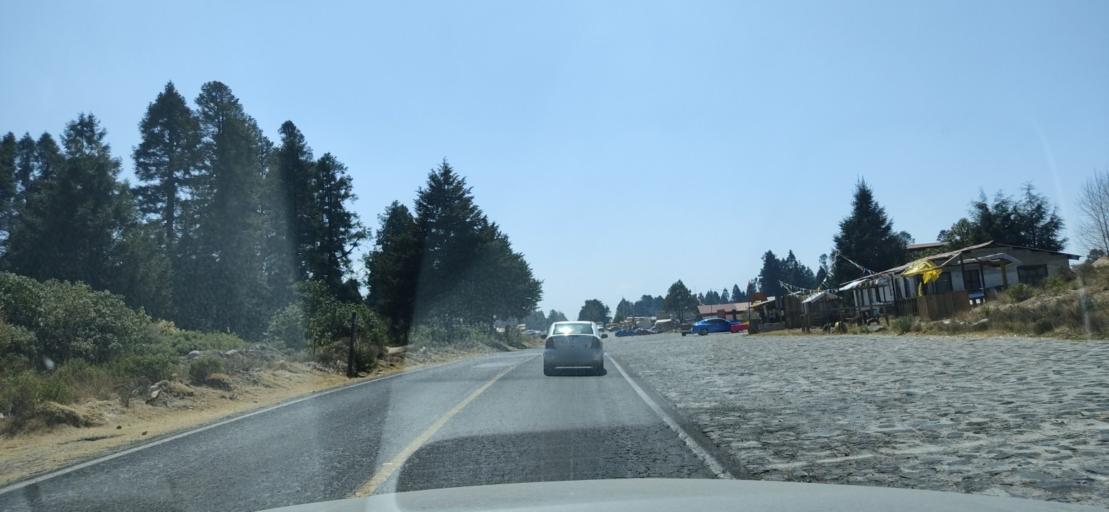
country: MX
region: Mexico
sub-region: Ocoyoacac
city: San Jeronimo Acazulco
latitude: 19.2723
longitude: -99.3759
